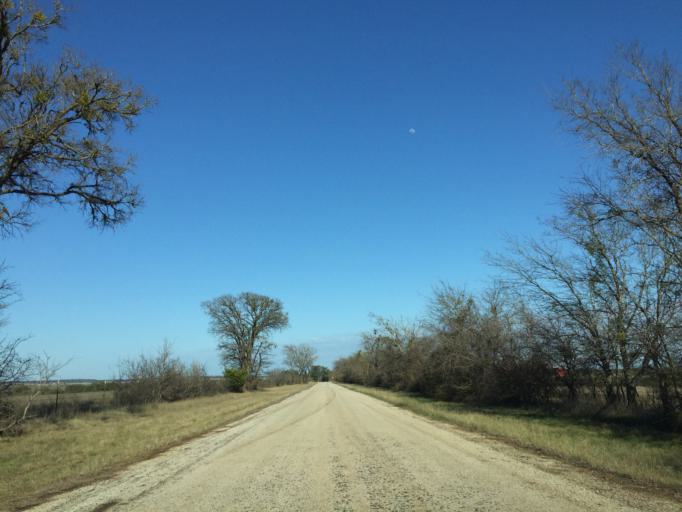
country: US
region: Texas
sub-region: Williamson County
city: Florence
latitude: 30.7756
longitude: -97.8449
